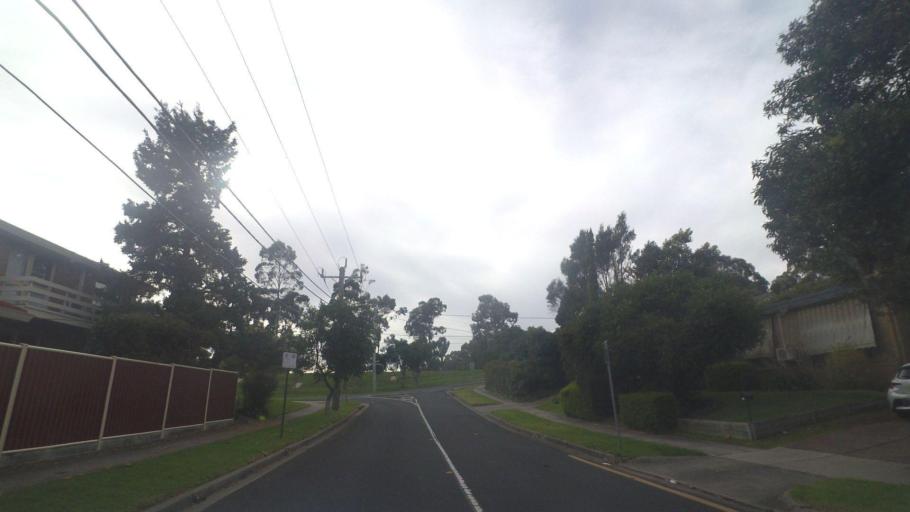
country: AU
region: Victoria
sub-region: Whitehorse
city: Vermont South
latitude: -37.8599
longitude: 145.1743
